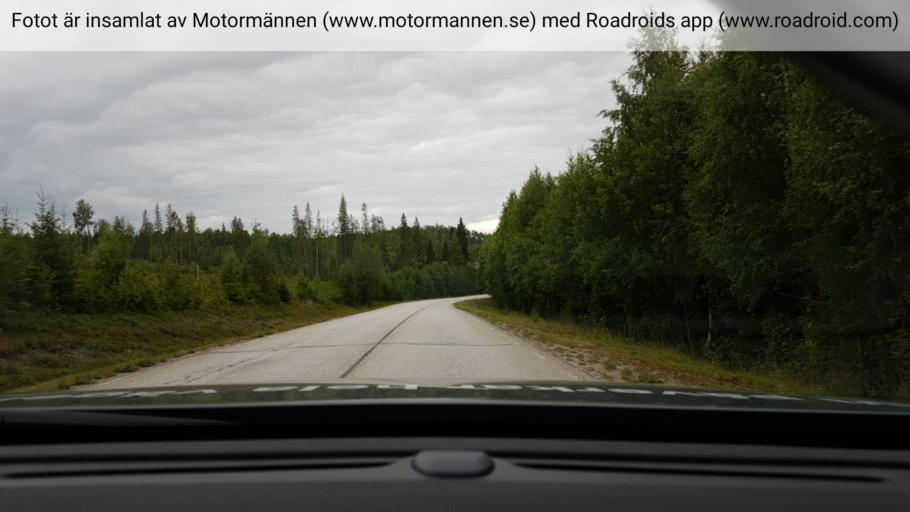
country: SE
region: Vaesterbotten
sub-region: Vannas Kommun
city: Vannasby
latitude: 64.0129
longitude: 19.9283
